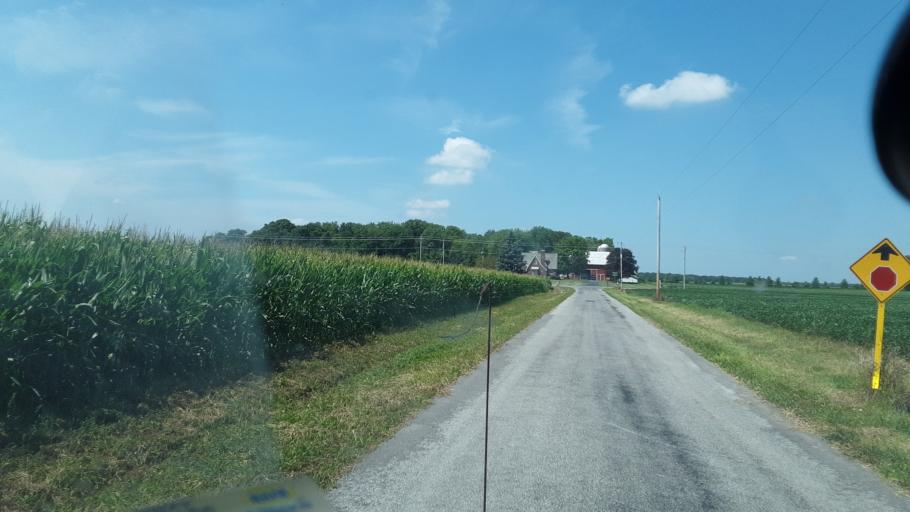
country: US
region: Ohio
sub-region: Hancock County
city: Findlay
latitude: 40.9748
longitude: -83.5531
